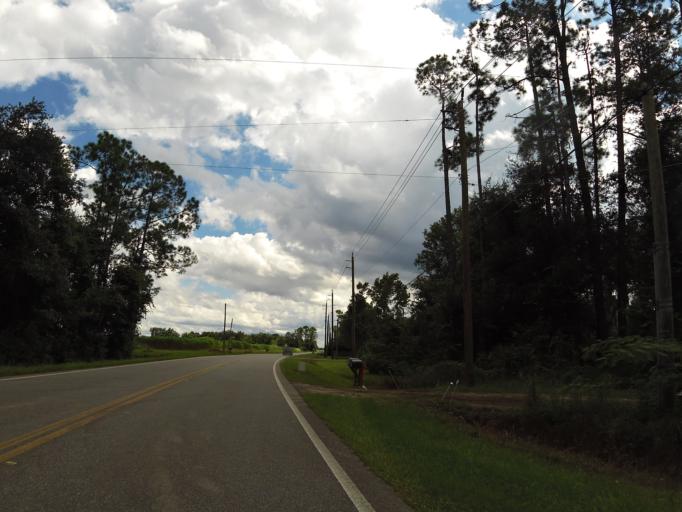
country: US
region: Florida
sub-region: Saint Johns County
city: Saint Augustine South
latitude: 29.8173
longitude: -81.4848
